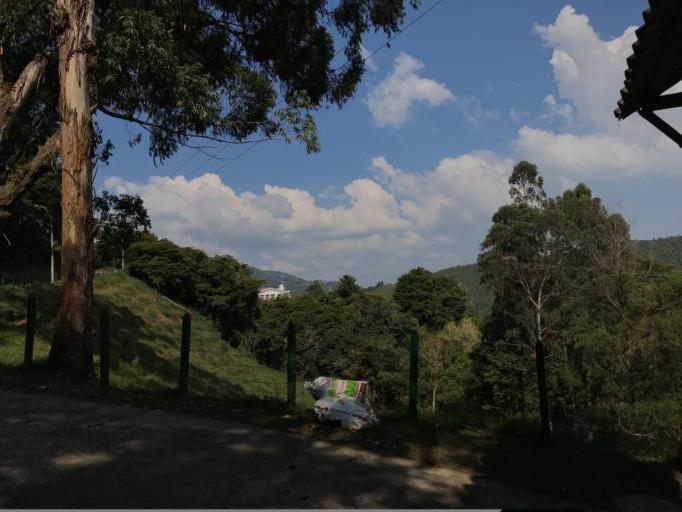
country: CO
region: Valle del Cauca
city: Cali
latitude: 3.4736
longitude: -76.6178
